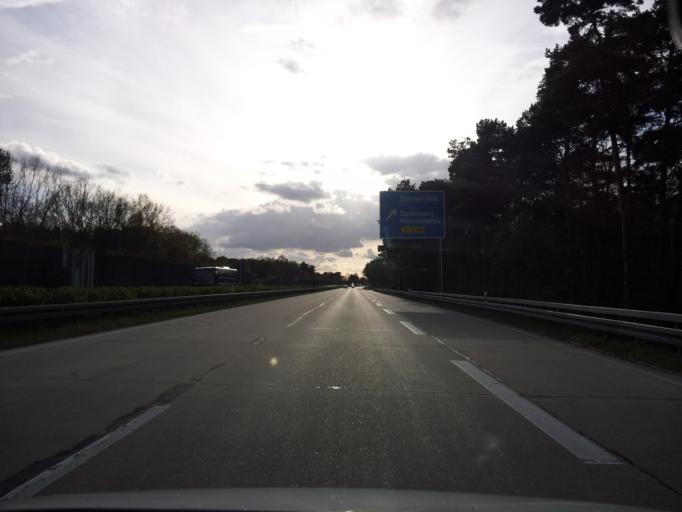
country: DE
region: Brandenburg
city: Cottbus
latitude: 51.7170
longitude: 14.3499
